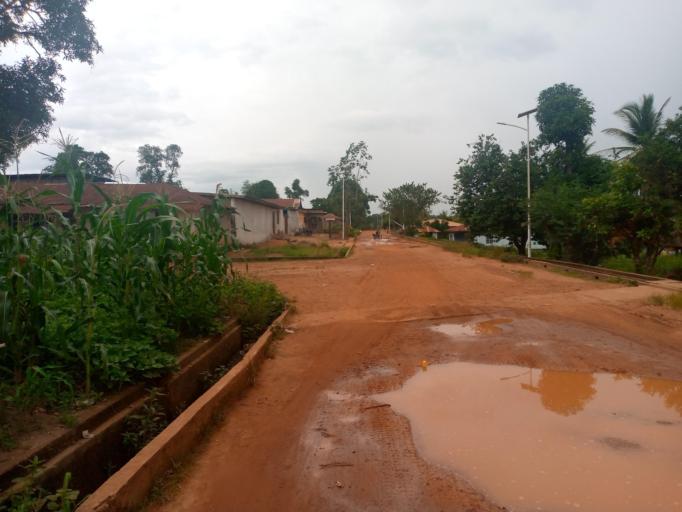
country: SL
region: Southern Province
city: Mogbwemo
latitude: 7.6073
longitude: -12.1751
